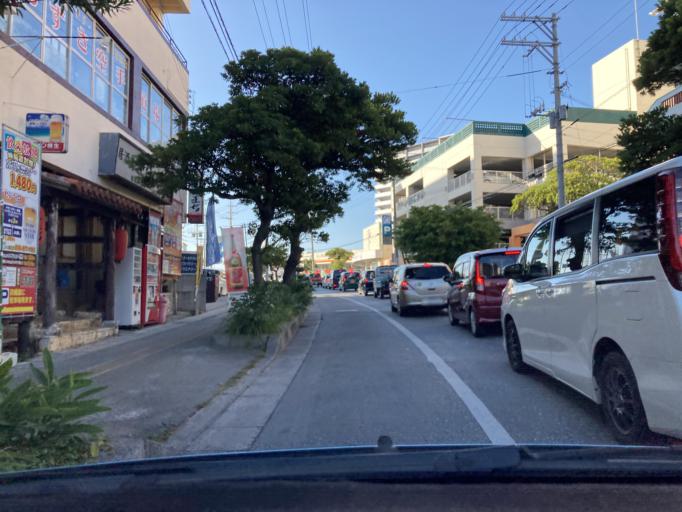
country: JP
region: Okinawa
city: Ginowan
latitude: 26.2582
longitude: 127.7126
